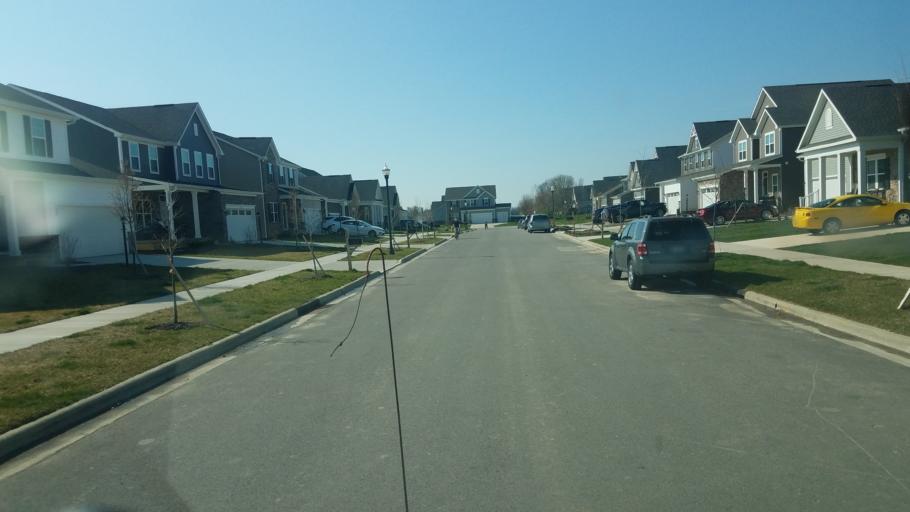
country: US
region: Ohio
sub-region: Delaware County
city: Delaware
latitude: 40.3040
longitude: -83.0398
